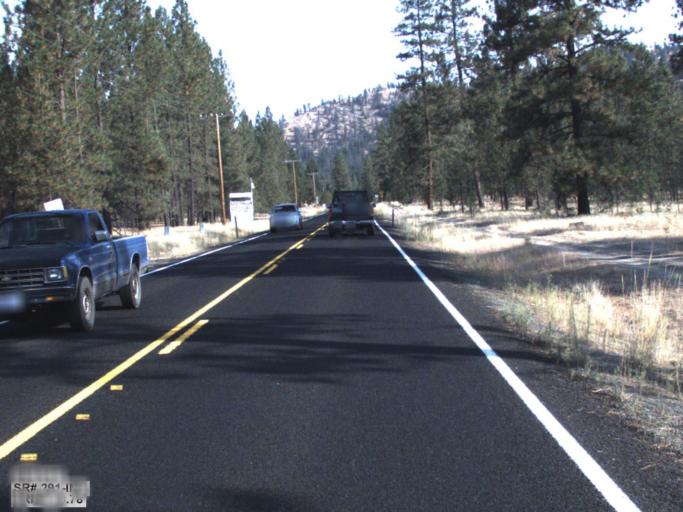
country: US
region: Washington
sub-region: Spokane County
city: Deer Park
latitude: 47.8652
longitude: -117.6479
